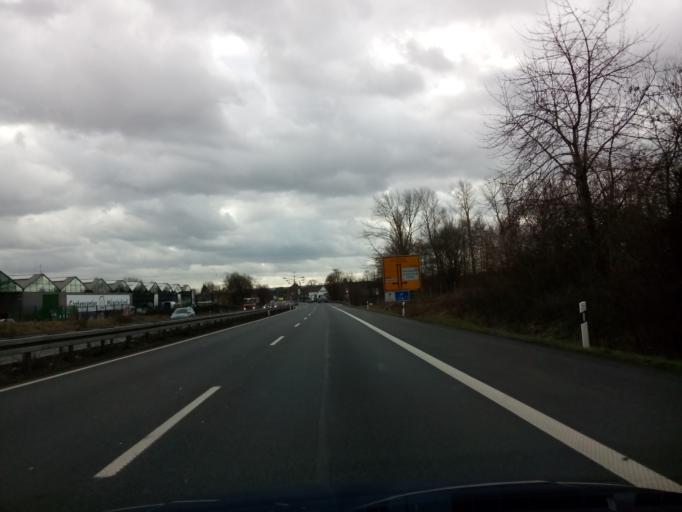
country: DE
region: Lower Saxony
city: Osnabrueck
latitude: 52.3057
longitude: 8.0344
